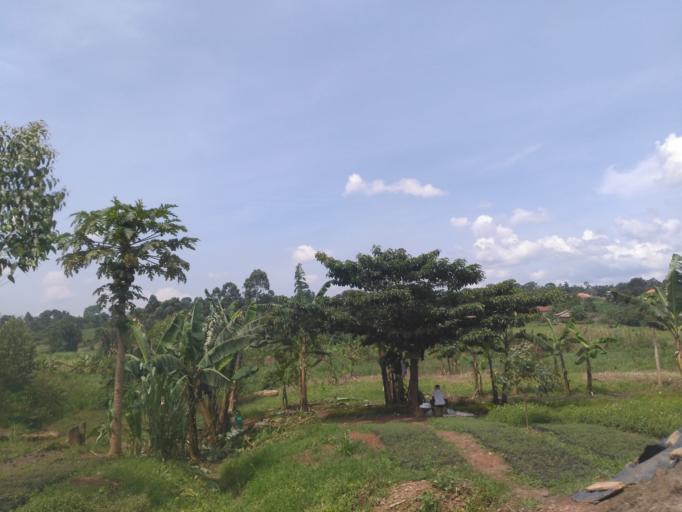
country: UG
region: Central Region
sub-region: Wakiso District
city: Bweyogerere
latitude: 0.4805
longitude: 32.6083
